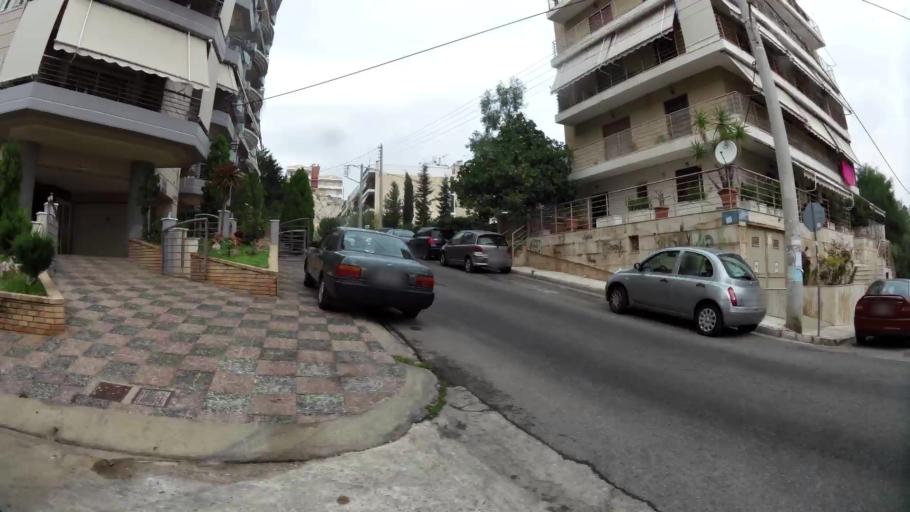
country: GR
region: Attica
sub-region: Nomos Piraios
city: Korydallos
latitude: 37.9833
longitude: 23.6318
